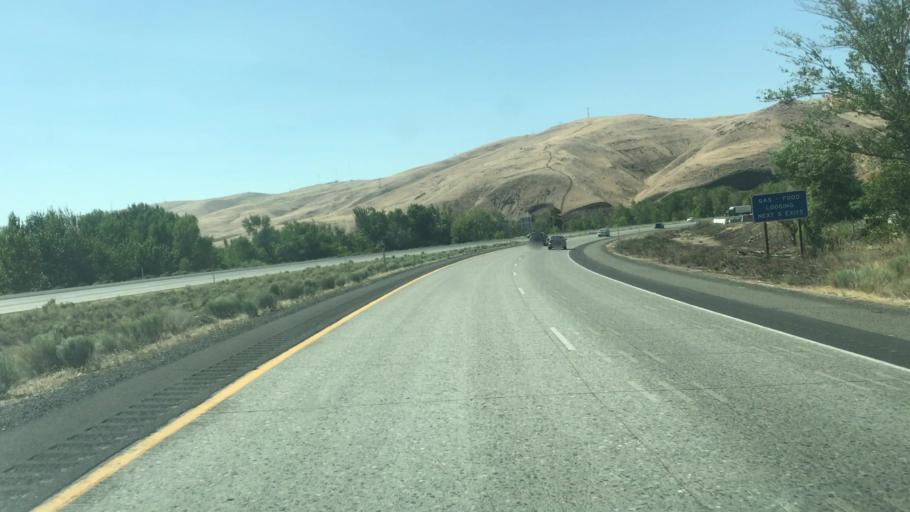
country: US
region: Washington
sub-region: Yakima County
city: Union Gap
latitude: 46.5210
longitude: -120.4671
